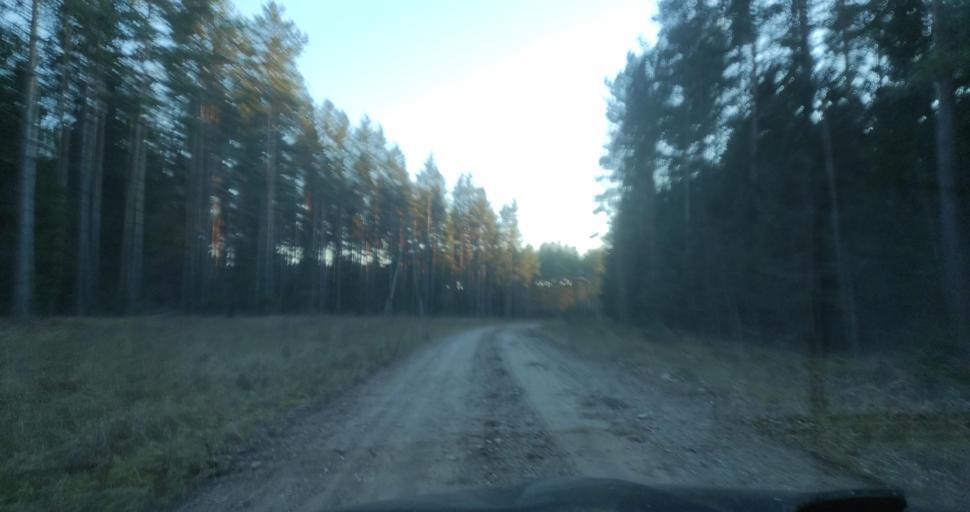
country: LV
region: Dundaga
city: Dundaga
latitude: 57.3739
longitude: 22.0784
